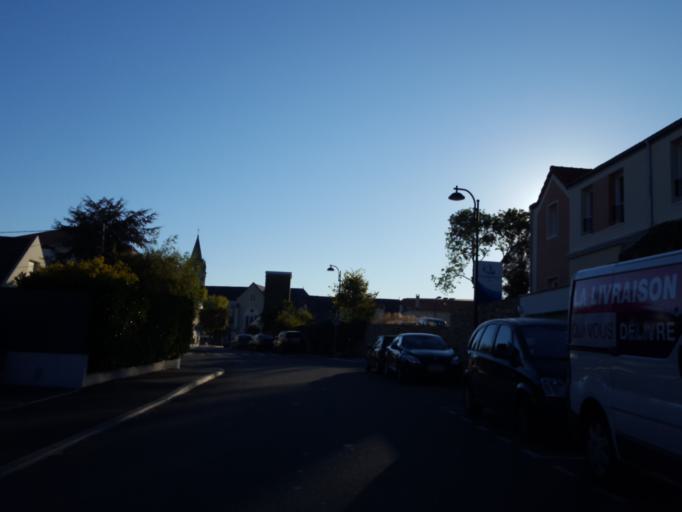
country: FR
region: Pays de la Loire
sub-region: Departement de la Loire-Atlantique
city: Basse-Goulaine
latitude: 47.2150
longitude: -1.4678
